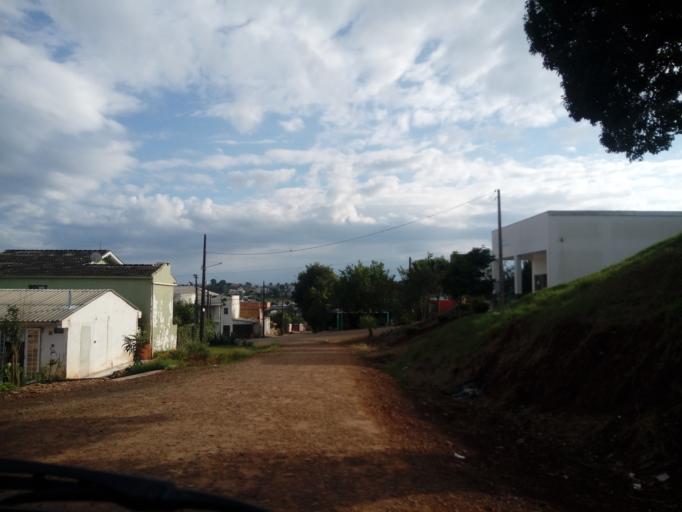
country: BR
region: Santa Catarina
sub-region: Chapeco
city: Chapeco
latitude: -27.1001
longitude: -52.5910
